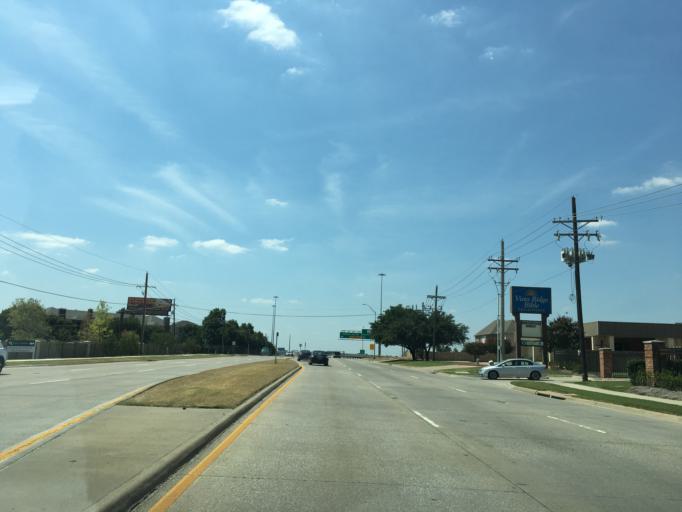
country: US
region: Texas
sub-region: Denton County
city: Lewisville
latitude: 33.0082
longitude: -96.9931
